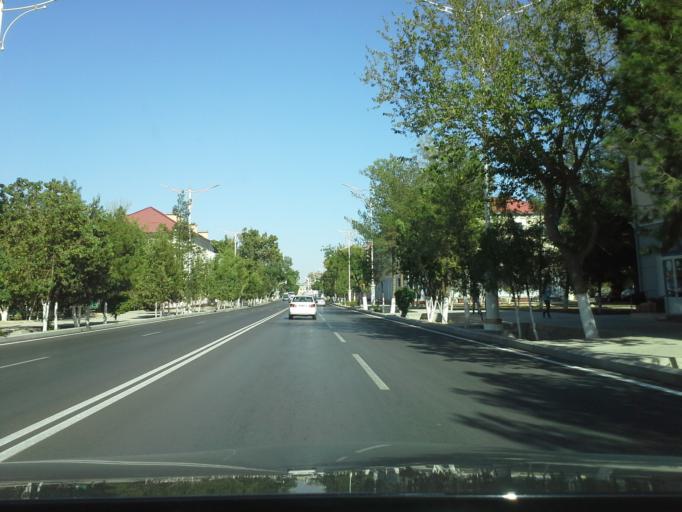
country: TM
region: Ahal
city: Ashgabat
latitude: 37.9581
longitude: 58.3509
